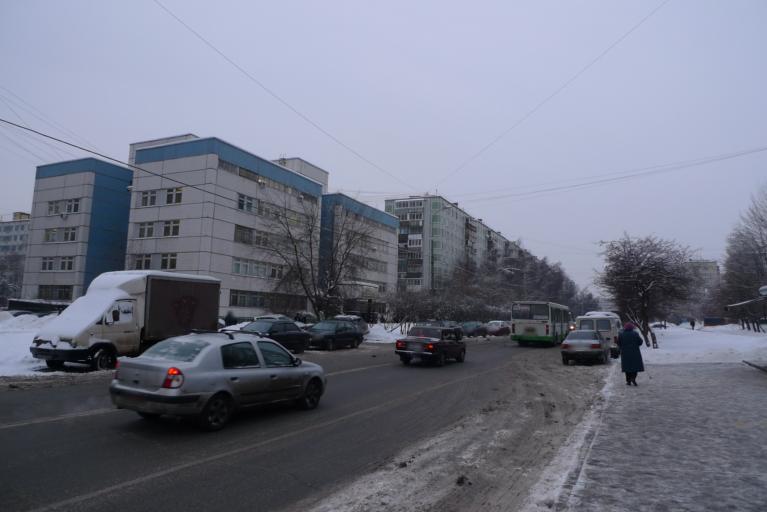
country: RU
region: Moscow
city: Orekhovo-Borisovo
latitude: 55.6045
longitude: 37.7132
